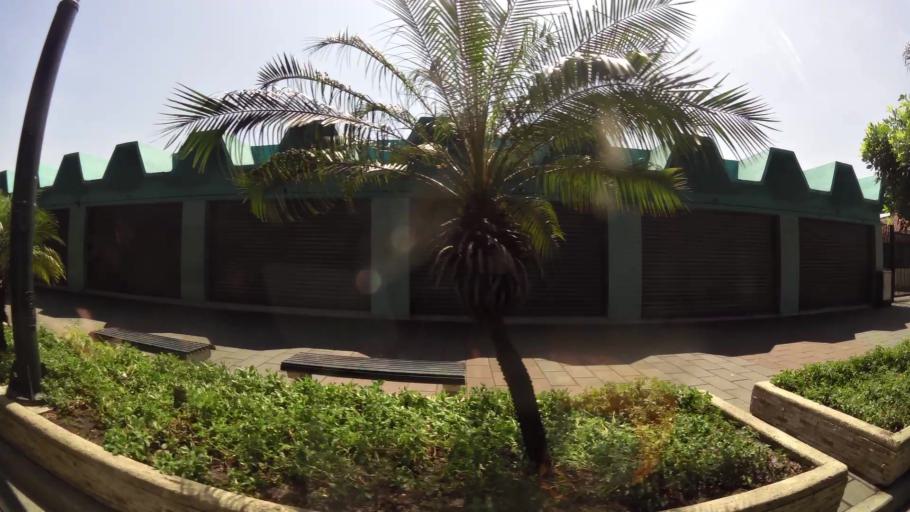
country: EC
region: Guayas
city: Guayaquil
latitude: -2.1811
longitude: -79.8935
